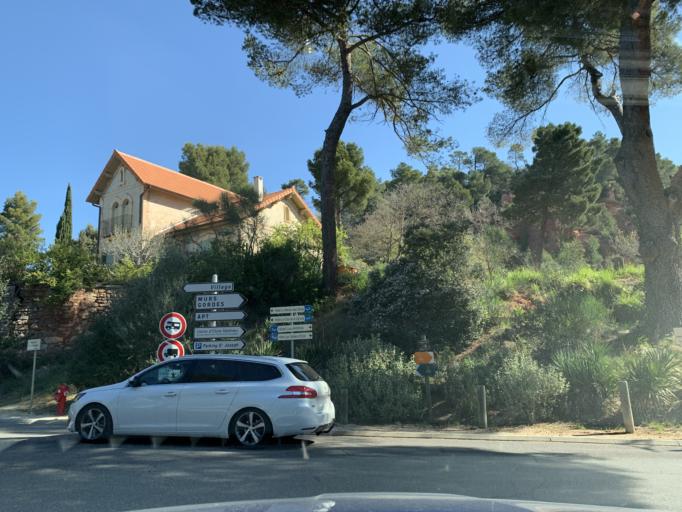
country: FR
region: Provence-Alpes-Cote d'Azur
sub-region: Departement du Vaucluse
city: Roussillon
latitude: 43.8977
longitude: 5.2940
